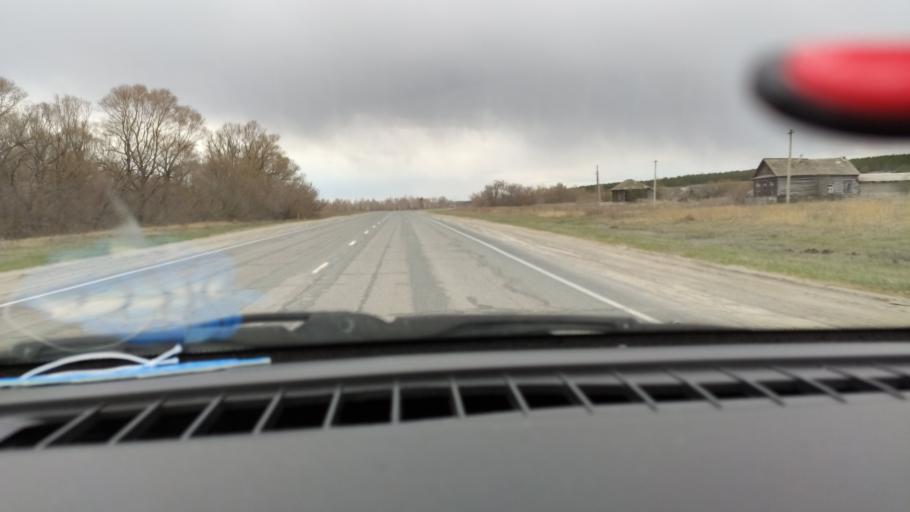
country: RU
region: Saratov
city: Sinodskoye
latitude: 52.0418
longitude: 46.7360
